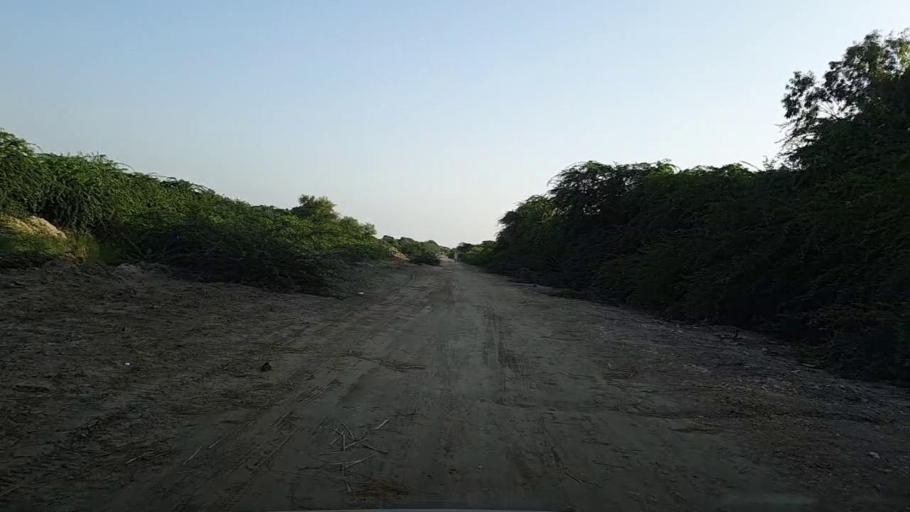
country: PK
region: Sindh
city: Kario
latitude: 24.7202
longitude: 68.6673
